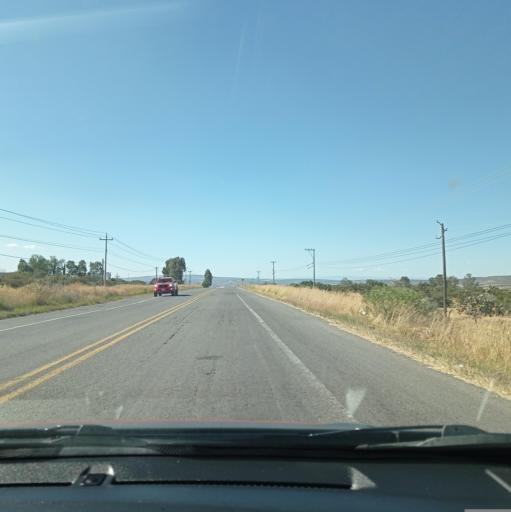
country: MX
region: Jalisco
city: San Miguel el Alto
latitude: 21.0151
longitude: -102.3250
